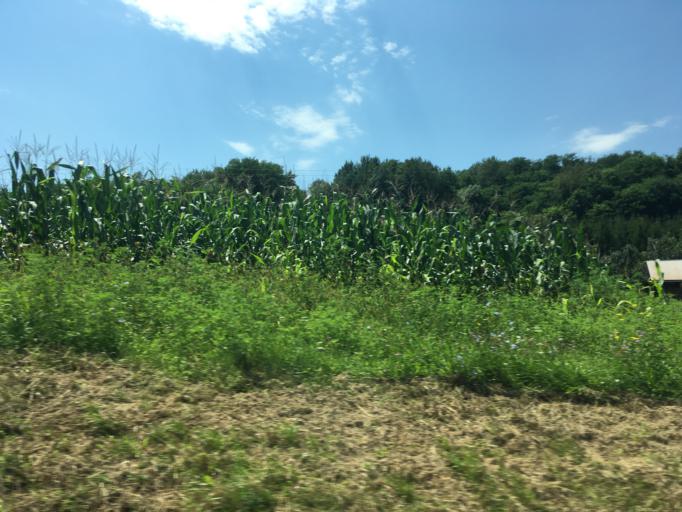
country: SI
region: Metlika
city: Metlika
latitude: 45.6047
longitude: 15.3324
